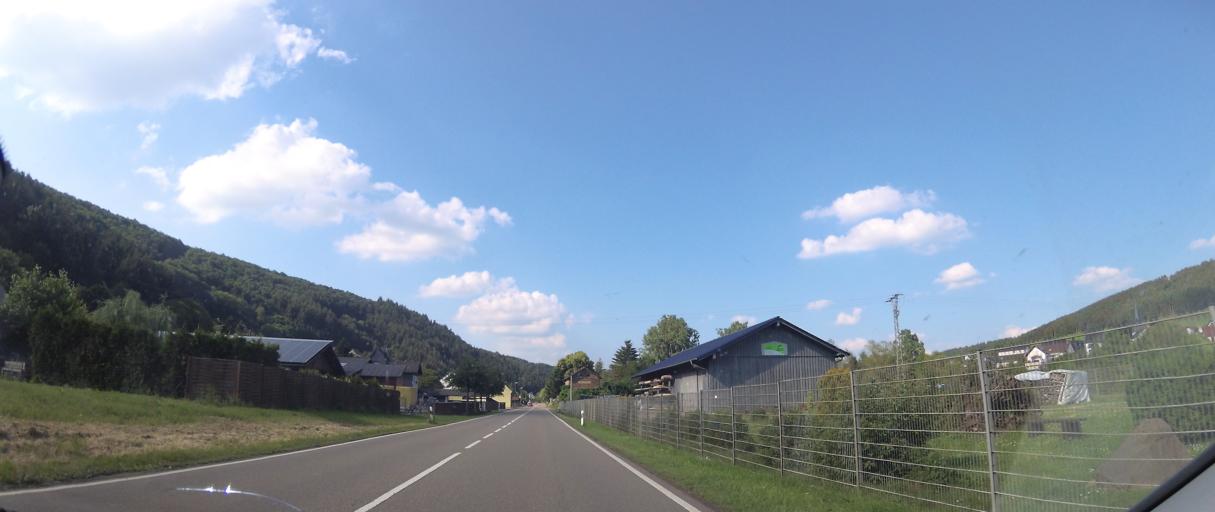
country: DE
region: Rheinland-Pfalz
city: Wiesweiler
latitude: 49.6363
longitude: 7.5690
